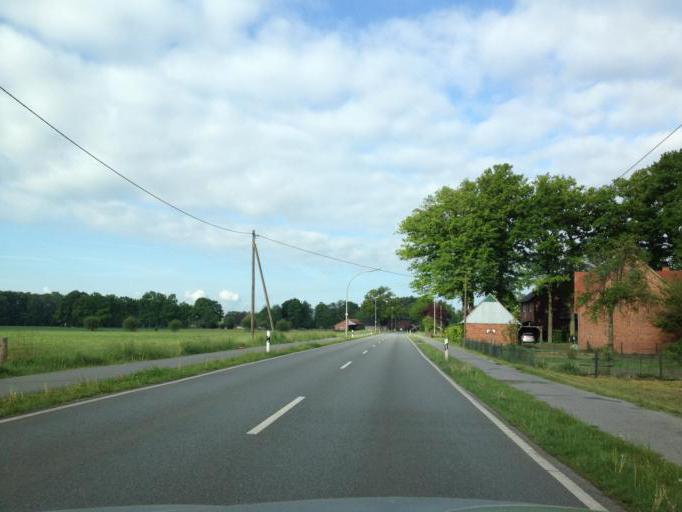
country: DE
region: North Rhine-Westphalia
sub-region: Regierungsbezirk Detmold
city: Guetersloh
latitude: 51.8824
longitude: 8.4148
